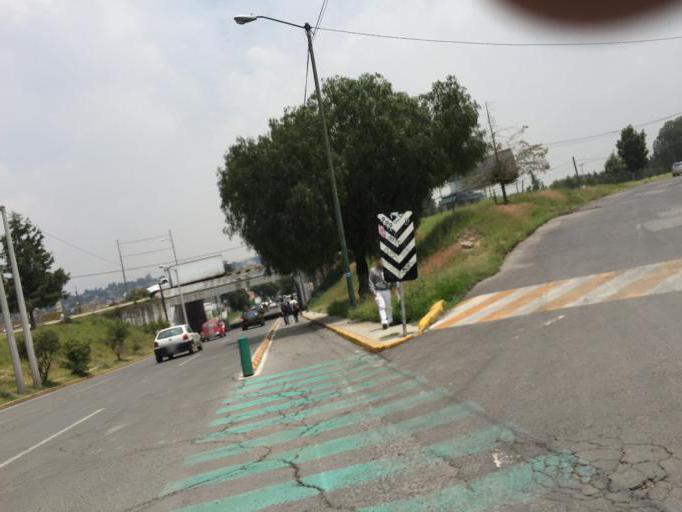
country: MX
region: Mexico
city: Cuautitlan Izcalli
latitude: 19.6418
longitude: -99.2075
